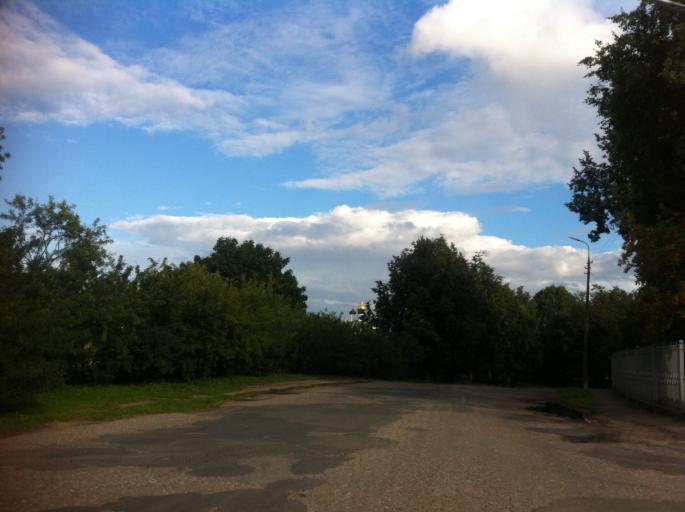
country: RU
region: Pskov
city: Pskov
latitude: 57.8261
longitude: 28.3182
